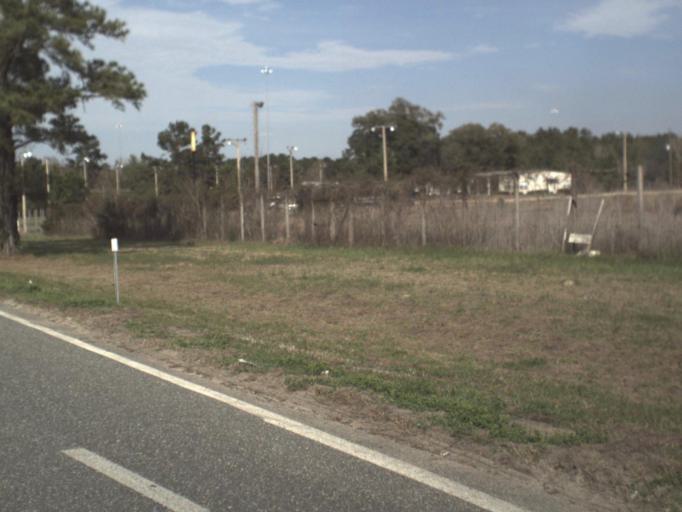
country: US
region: Florida
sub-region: Jefferson County
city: Monticello
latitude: 30.4731
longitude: -83.8907
